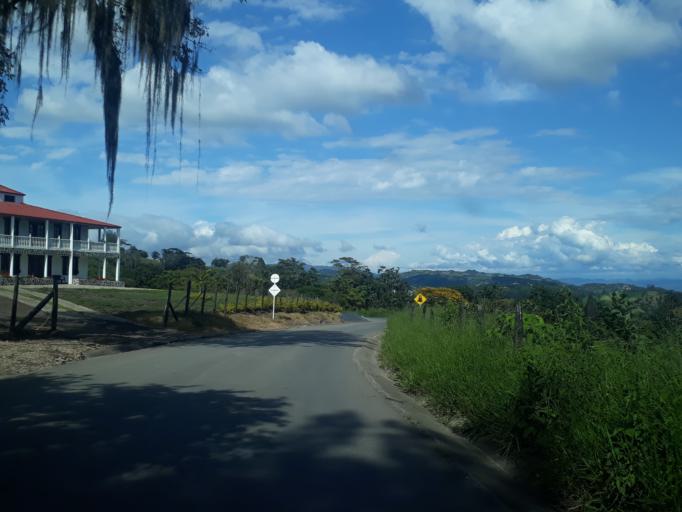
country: CO
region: Santander
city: Velez
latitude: 6.0490
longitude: -73.6528
